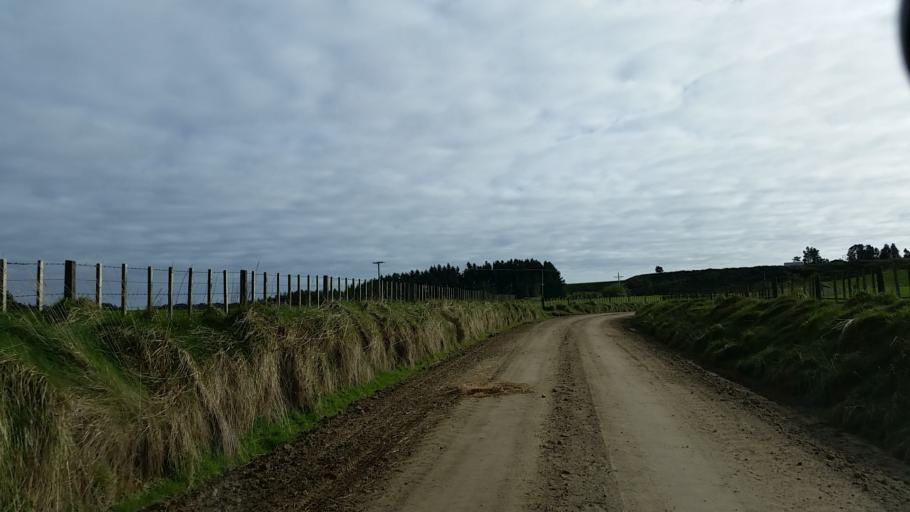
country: NZ
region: Taranaki
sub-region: South Taranaki District
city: Patea
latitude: -39.6949
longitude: 174.6578
